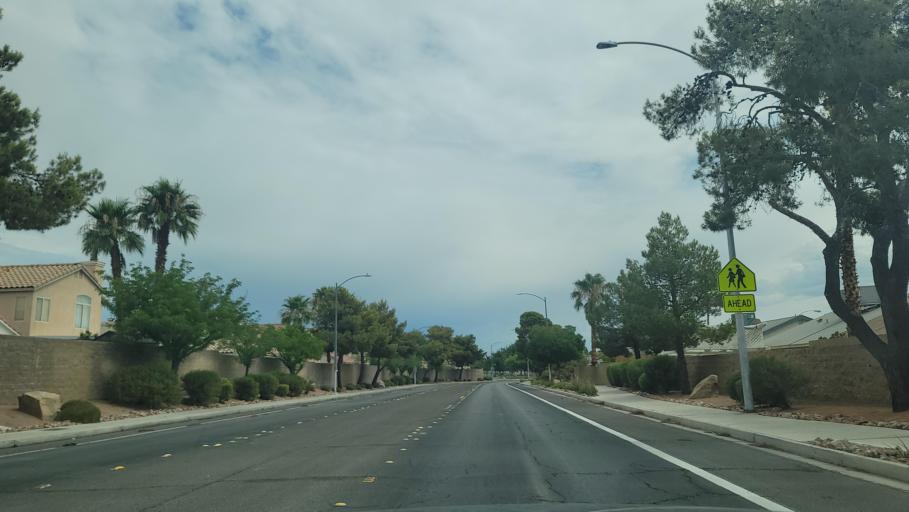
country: US
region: Nevada
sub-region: Clark County
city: Spring Valley
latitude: 36.1087
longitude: -115.2485
